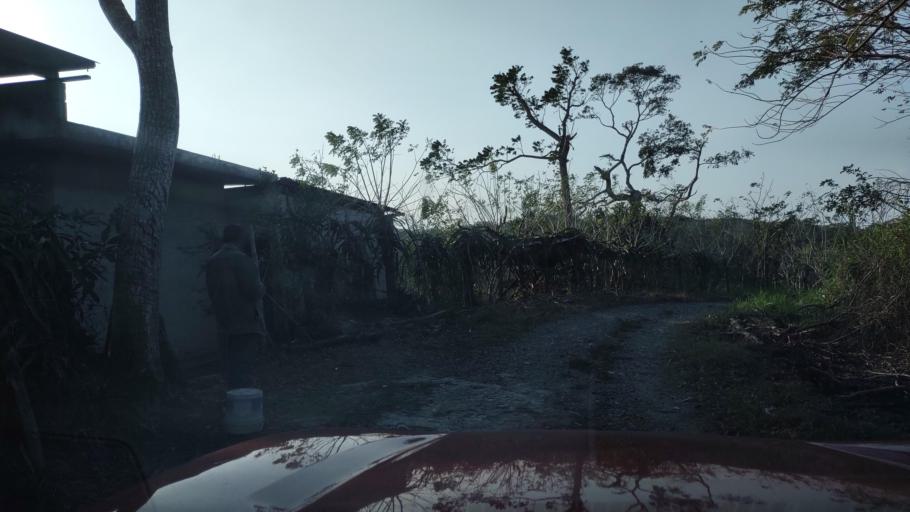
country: MX
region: Veracruz
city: Papantla de Olarte
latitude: 20.4595
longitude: -97.3714
